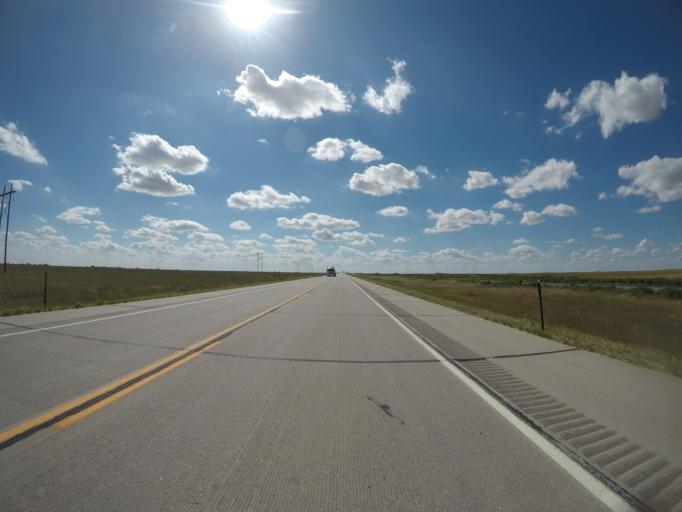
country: US
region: Colorado
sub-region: Phillips County
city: Holyoke
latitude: 40.6016
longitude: -102.4068
